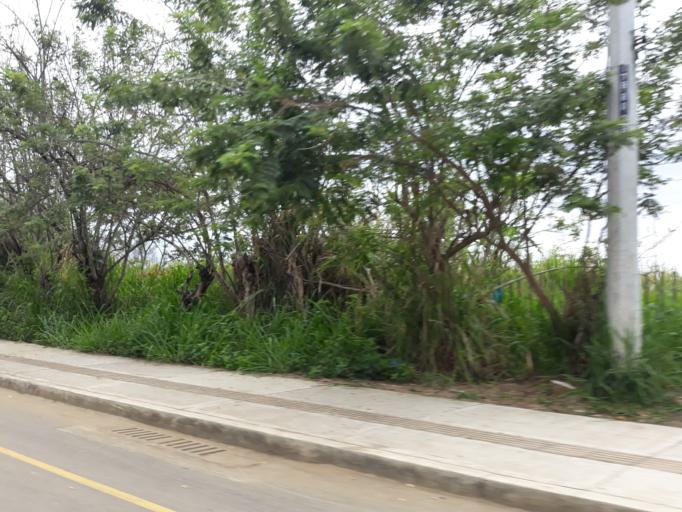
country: CO
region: Valle del Cauca
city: Jamundi
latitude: 3.3457
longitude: -76.5505
